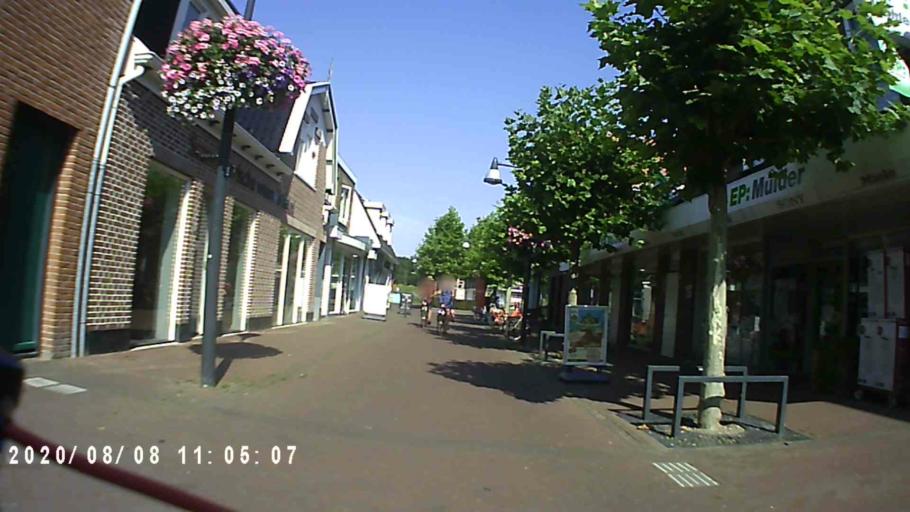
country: NL
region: Groningen
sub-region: Gemeente Leek
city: Leek
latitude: 53.1631
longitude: 6.3913
